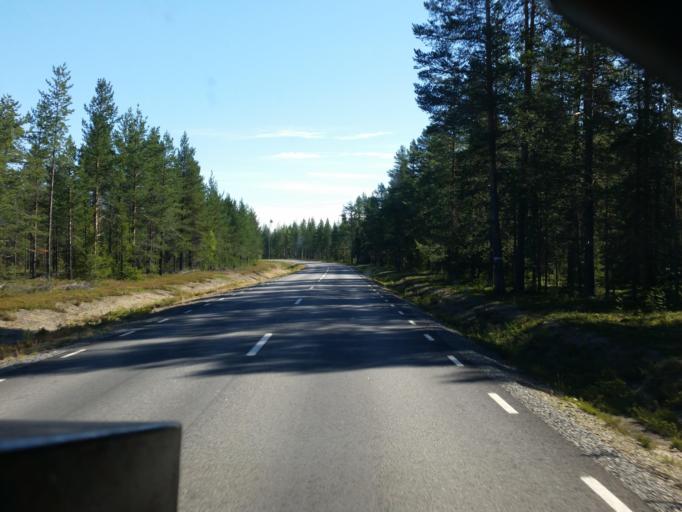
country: SE
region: Vaesterbotten
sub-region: Skelleftea Kommun
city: Storvik
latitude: 65.3356
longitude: 20.8822
